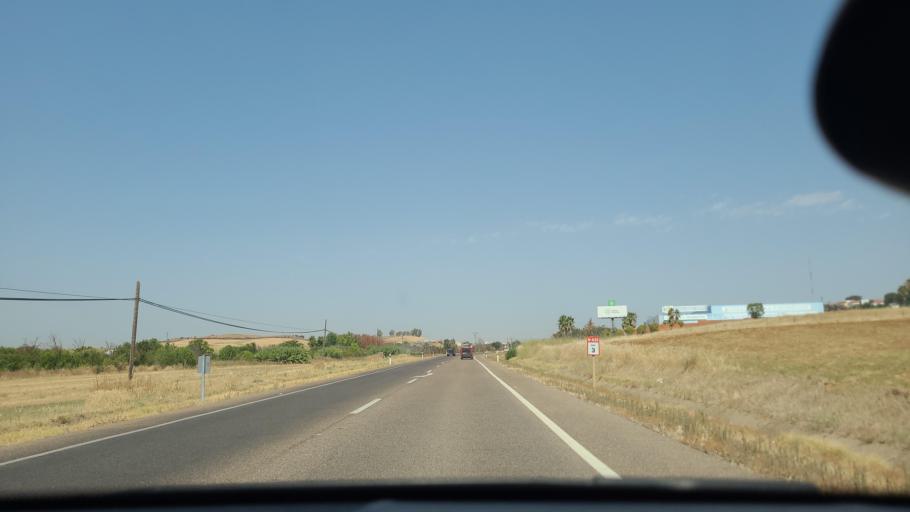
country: ES
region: Extremadura
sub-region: Provincia de Badajoz
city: Badajoz
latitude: 38.8517
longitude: -6.9415
